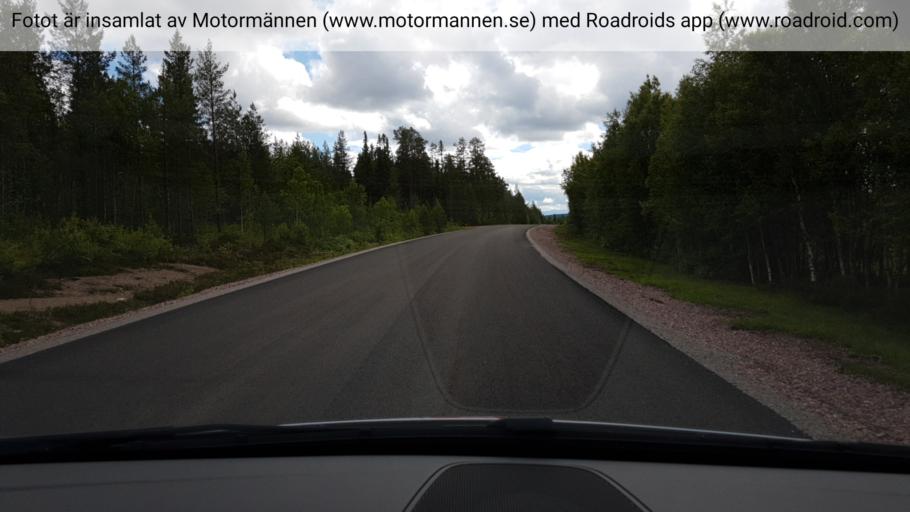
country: SE
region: Dalarna
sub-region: Alvdalens Kommun
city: AElvdalen
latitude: 61.6327
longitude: 14.1847
